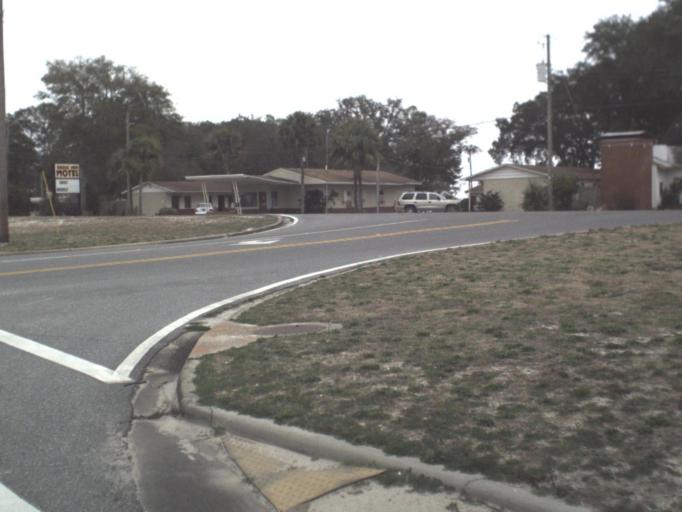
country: US
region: Florida
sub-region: Bay County
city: Parker
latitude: 30.1111
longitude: -85.6024
